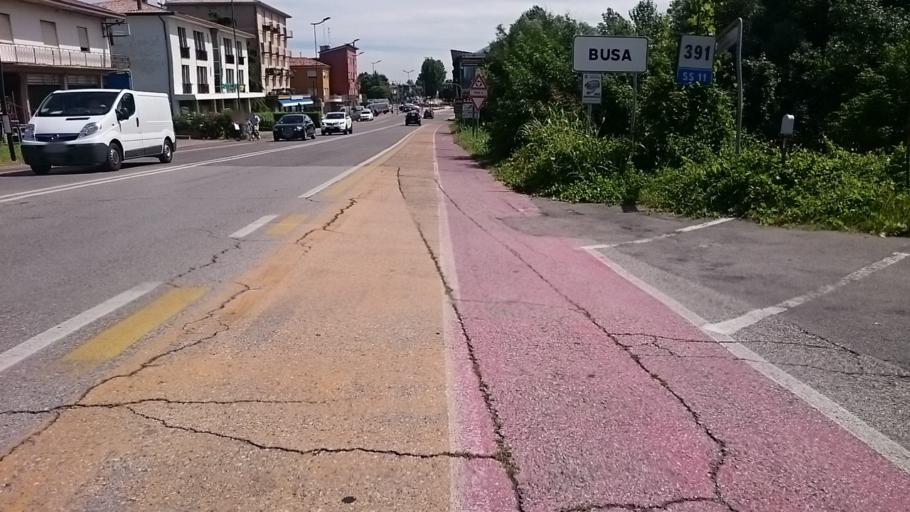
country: IT
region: Veneto
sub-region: Provincia di Padova
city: San Vito
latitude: 45.4276
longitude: 11.9523
